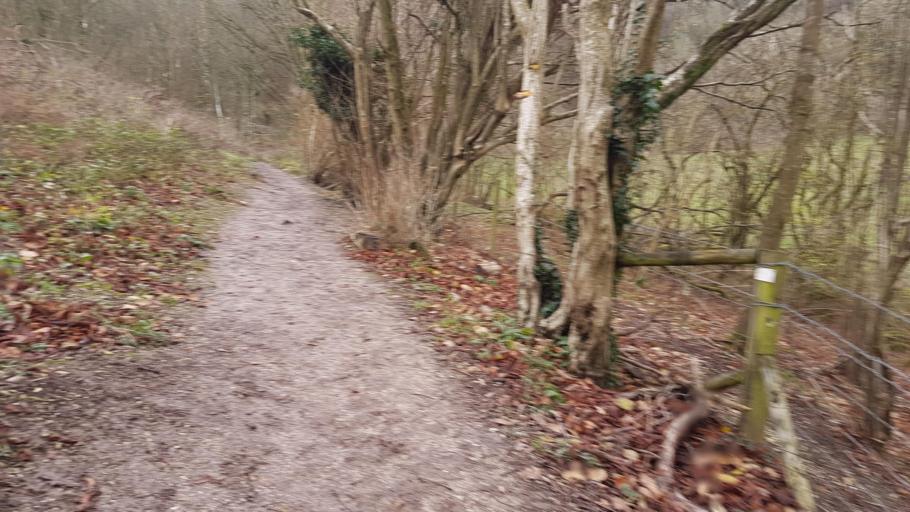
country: GB
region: England
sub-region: West Sussex
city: Steyning
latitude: 50.8830
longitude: -0.3459
